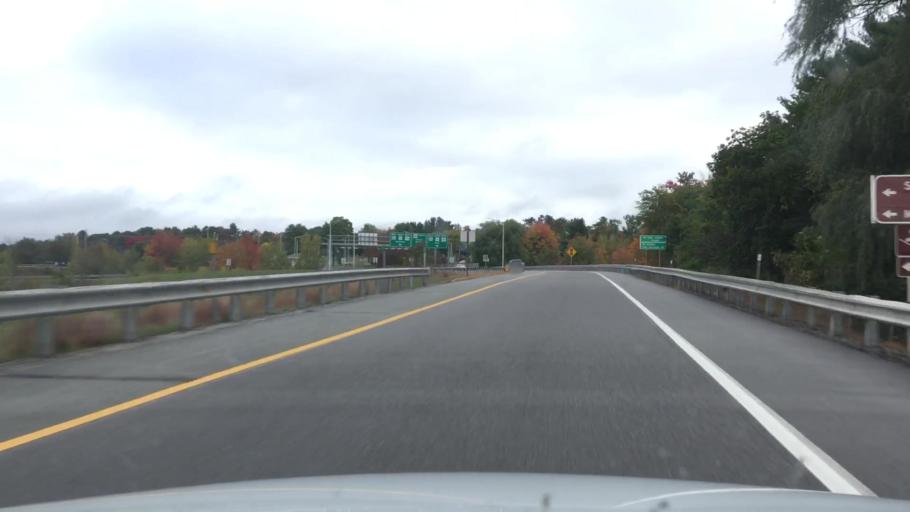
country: US
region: Maine
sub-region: Cumberland County
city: New Gloucester
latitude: 43.8809
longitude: -70.3335
